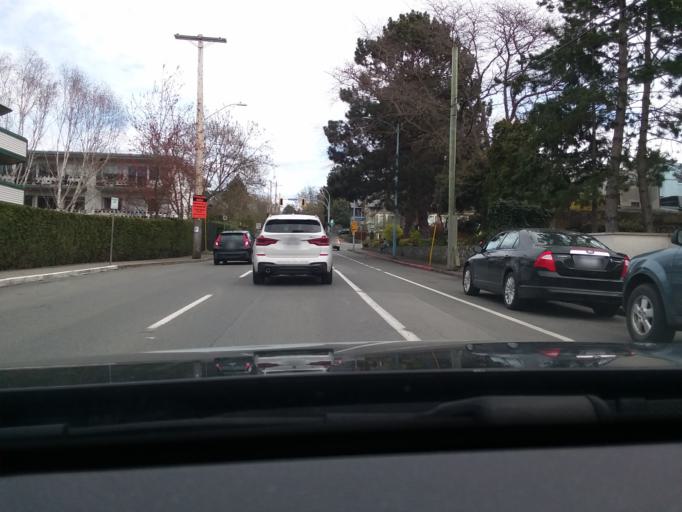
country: CA
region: British Columbia
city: Victoria
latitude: 48.4255
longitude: -123.3485
